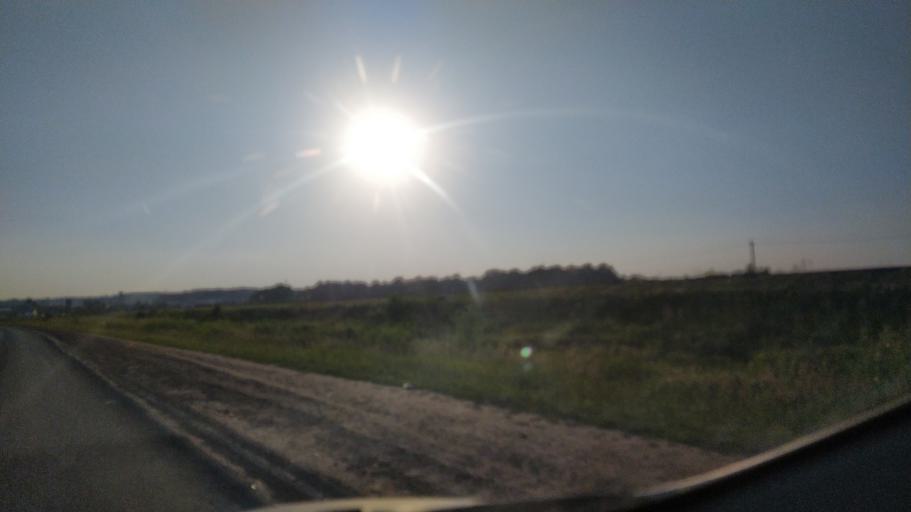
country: RU
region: Chuvashia
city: Kugesi
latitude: 56.0407
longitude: 47.3288
